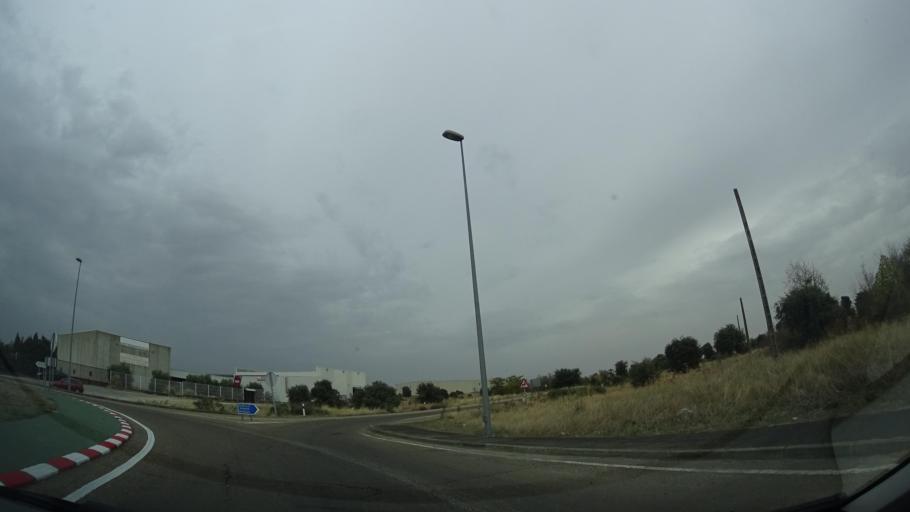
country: ES
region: Extremadura
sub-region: Provincia de Caceres
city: Trujillo
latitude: 39.4822
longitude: -5.8530
